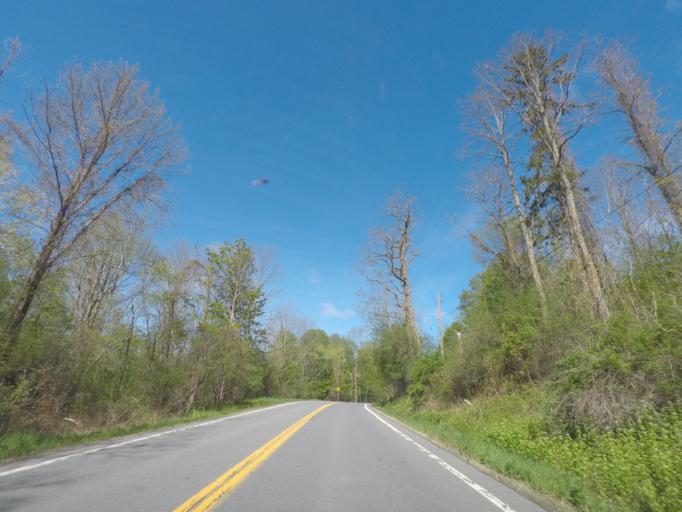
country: US
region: New York
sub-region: Albany County
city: Ravena
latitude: 42.4824
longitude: -73.9281
